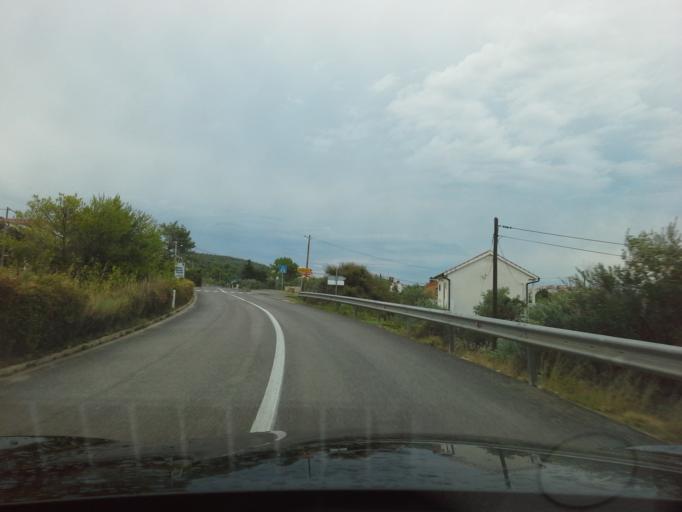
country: HR
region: Primorsko-Goranska
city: Banjol
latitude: 44.7278
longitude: 14.8151
